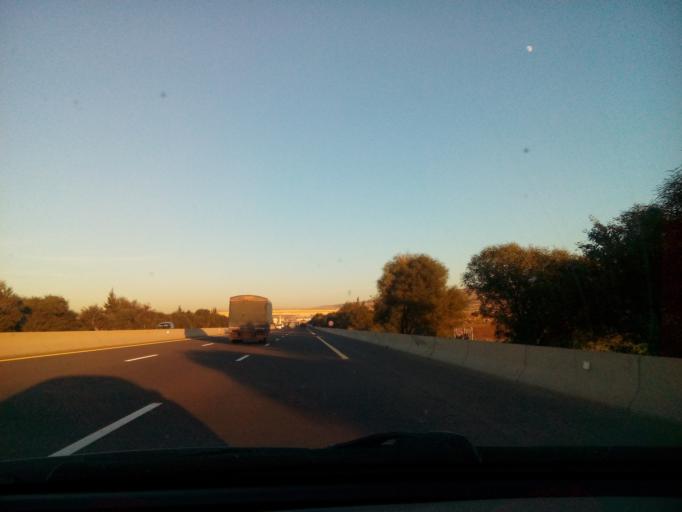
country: DZ
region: Relizane
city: Oued Rhiou
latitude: 35.9894
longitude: 0.9673
